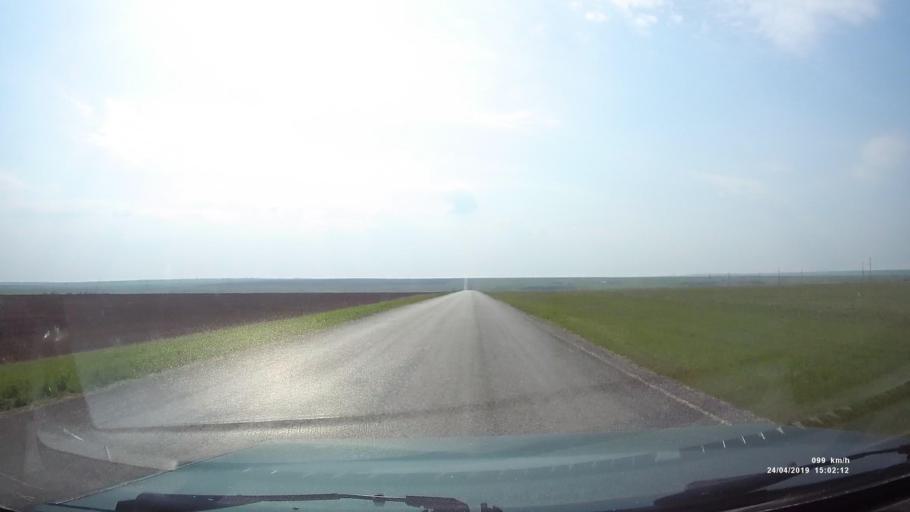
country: RU
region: Rostov
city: Remontnoye
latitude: 46.5663
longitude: 43.5174
